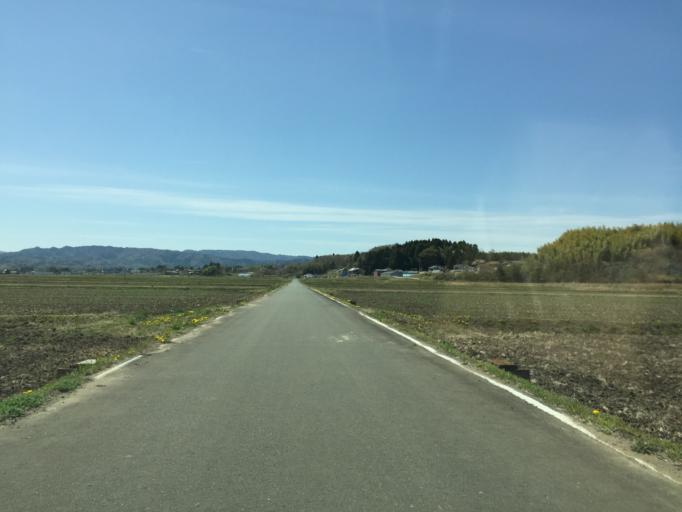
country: JP
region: Miyagi
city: Marumori
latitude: 37.7747
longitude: 140.9547
